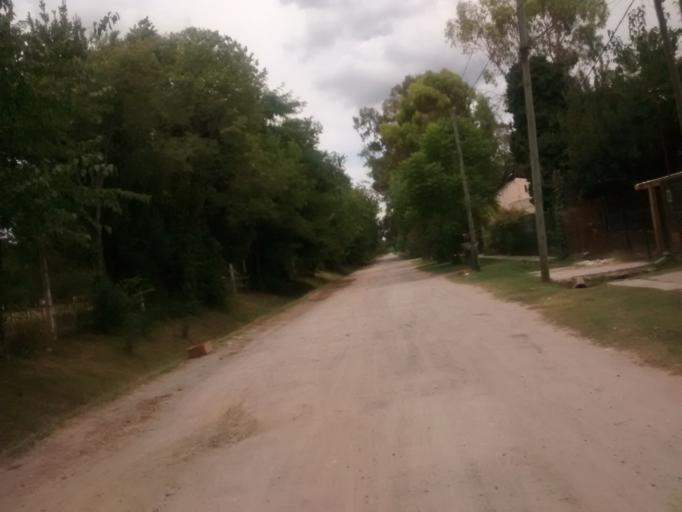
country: AR
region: Buenos Aires
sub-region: Partido de La Plata
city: La Plata
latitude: -34.8589
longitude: -58.0720
